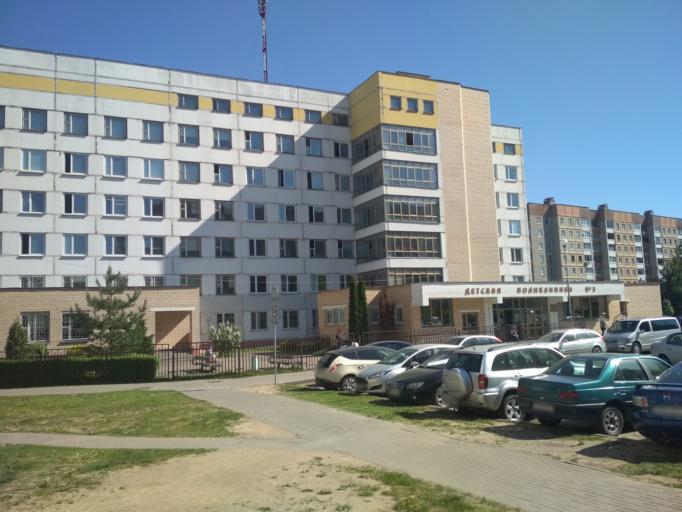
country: BY
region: Minsk
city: Minsk
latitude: 53.8811
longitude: 27.5396
